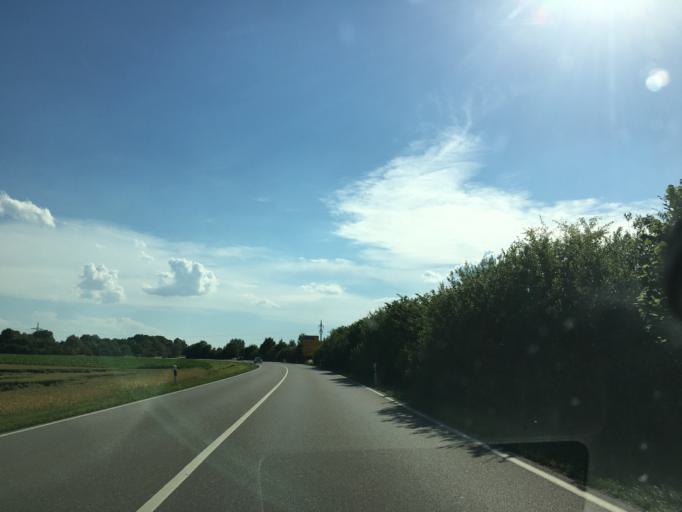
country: DE
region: Bavaria
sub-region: Upper Bavaria
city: Stammham
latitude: 48.2915
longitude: 11.8706
